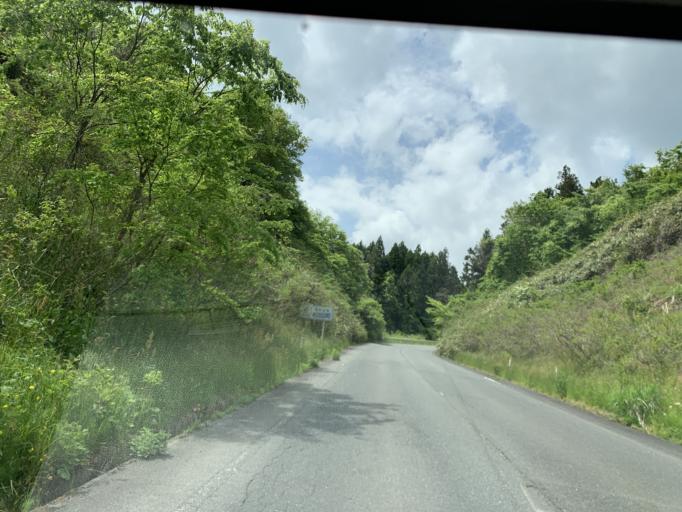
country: JP
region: Miyagi
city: Furukawa
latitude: 38.7211
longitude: 140.9227
